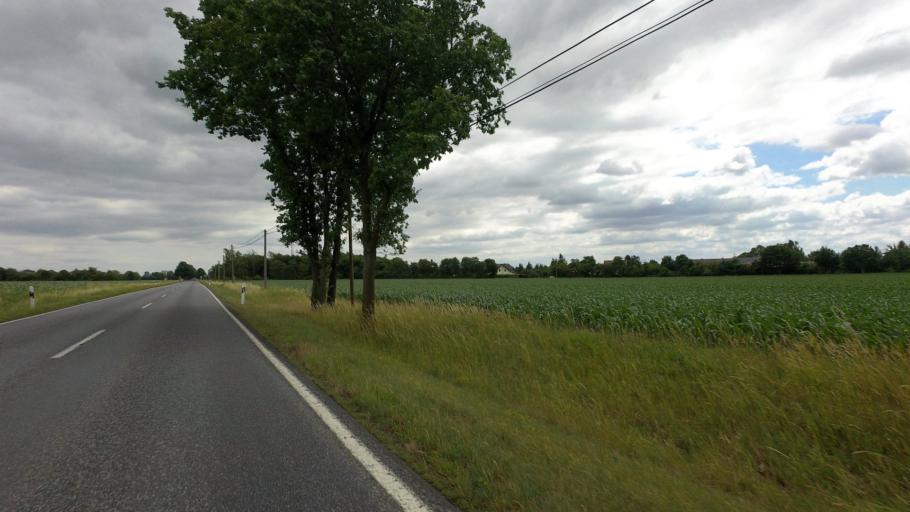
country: DE
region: Brandenburg
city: Luckau
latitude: 51.8250
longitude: 13.7889
